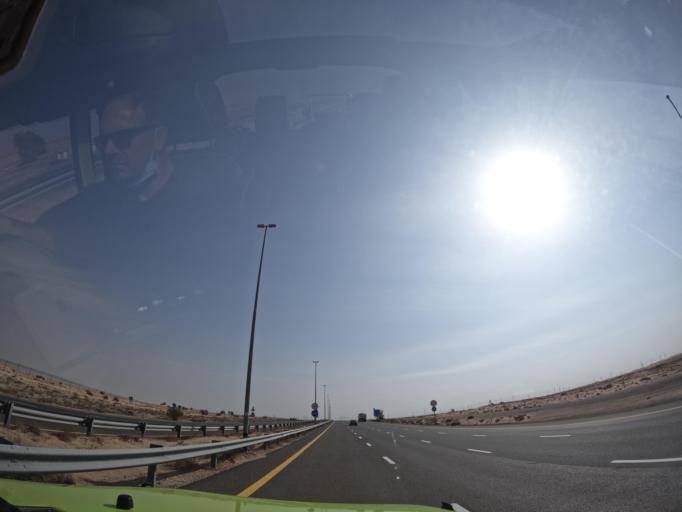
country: AE
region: Ash Shariqah
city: Sharjah
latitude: 25.0110
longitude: 55.5180
